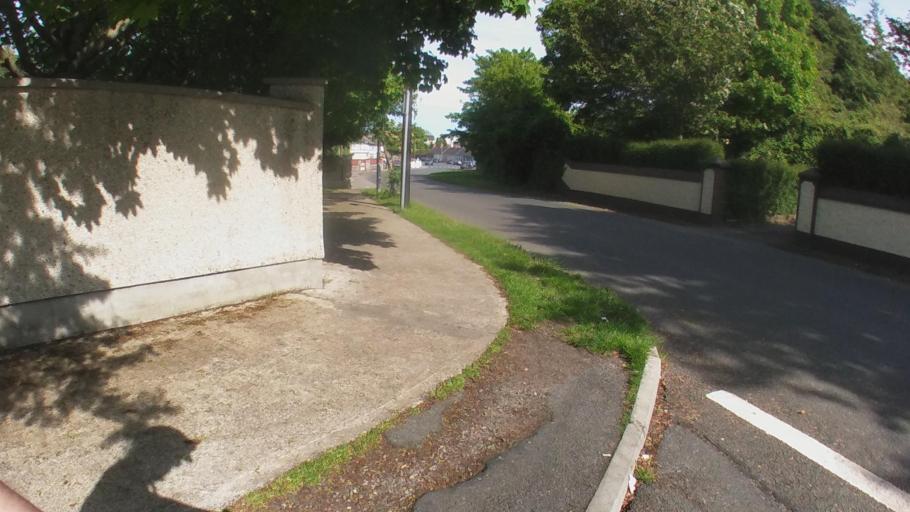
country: IE
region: Leinster
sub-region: County Carlow
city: Carlow
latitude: 52.8349
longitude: -6.9433
